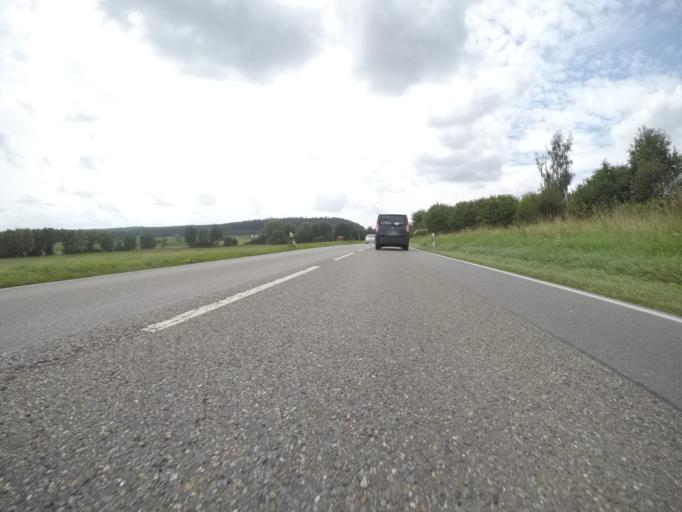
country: DE
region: Baden-Wuerttemberg
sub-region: Regierungsbezirk Stuttgart
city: Nufringen
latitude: 48.6290
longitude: 8.9004
